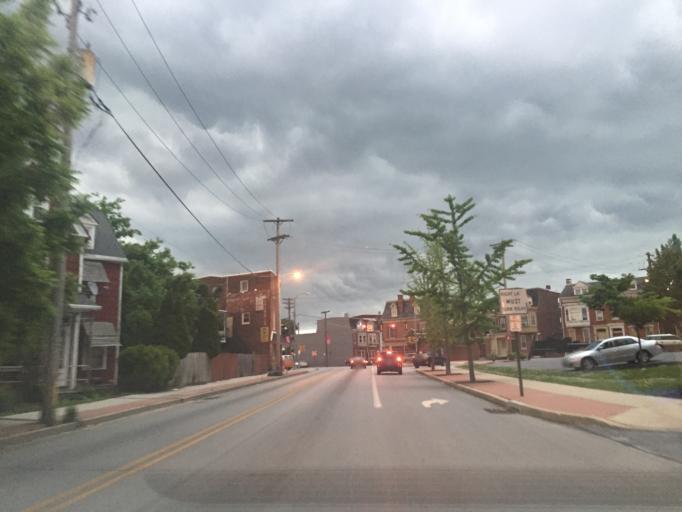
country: US
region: Pennsylvania
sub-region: York County
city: York
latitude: 39.9614
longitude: -76.7389
